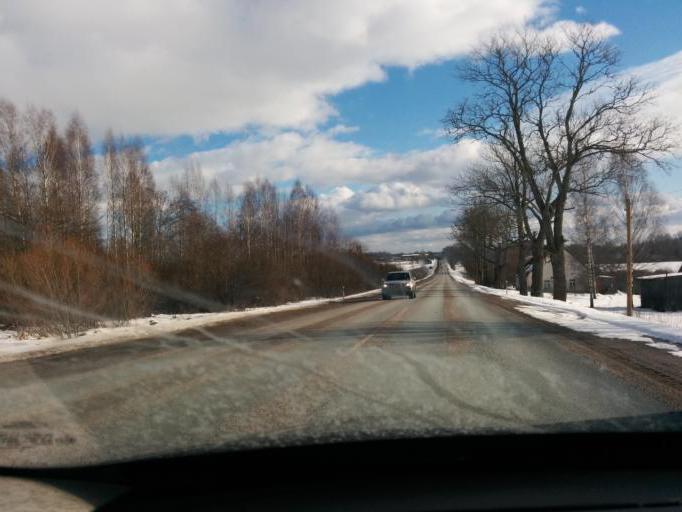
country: LV
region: Gulbenes Rajons
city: Gulbene
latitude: 57.1894
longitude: 26.7216
